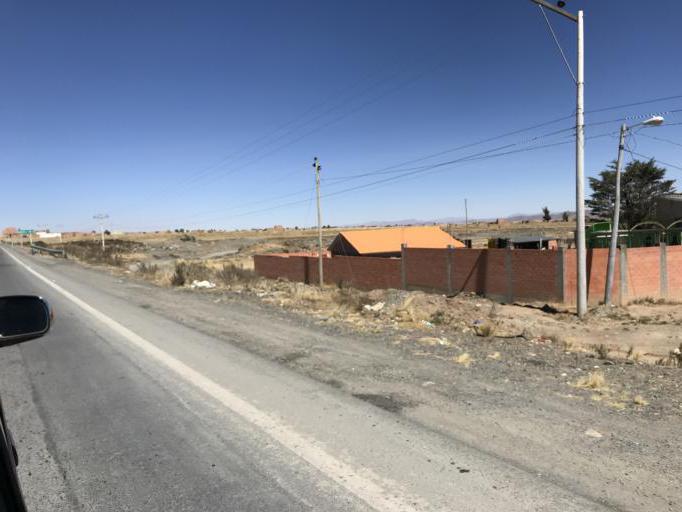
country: BO
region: La Paz
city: Batallas
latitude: -16.3284
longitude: -68.4239
